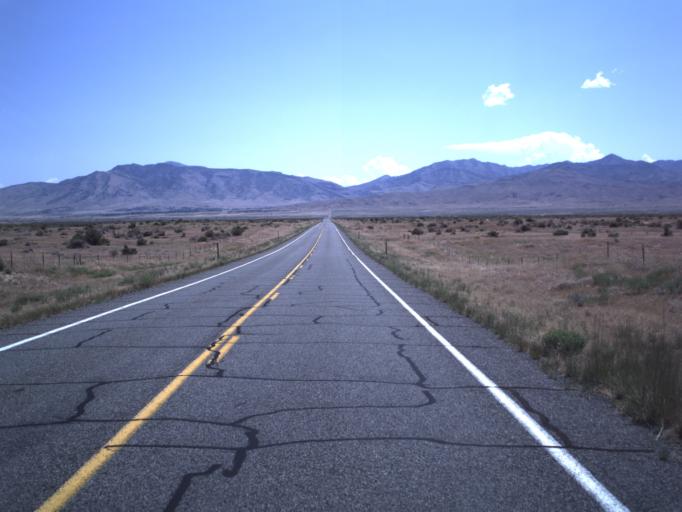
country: US
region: Utah
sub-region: Millard County
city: Delta
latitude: 39.3534
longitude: -112.4687
